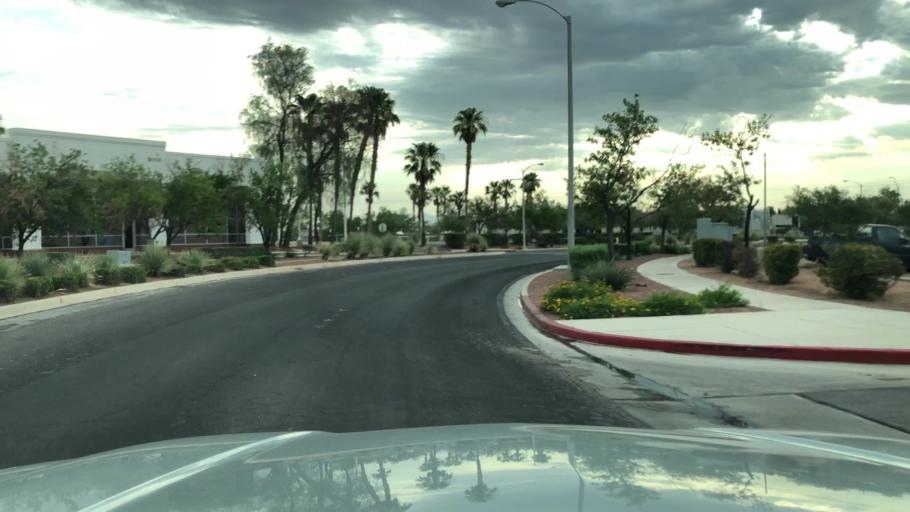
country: US
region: Nevada
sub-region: Clark County
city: Whitney
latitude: 36.0729
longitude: -115.0748
